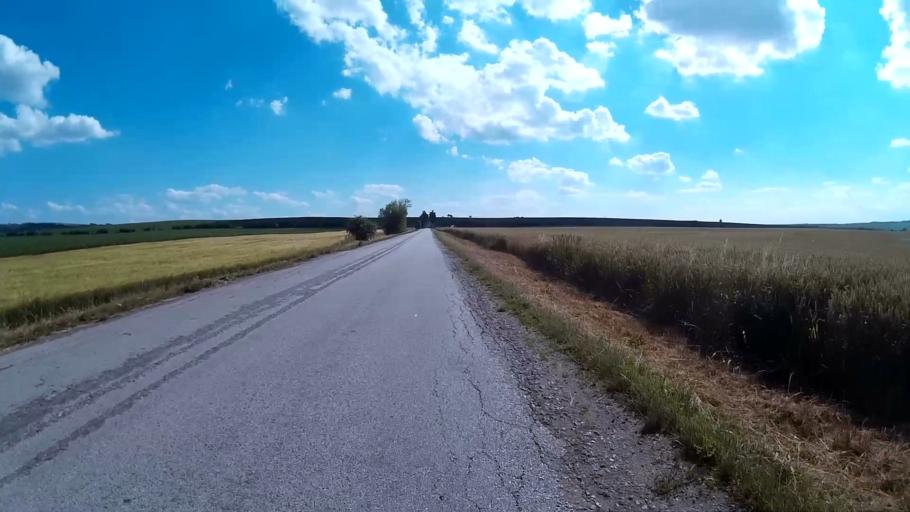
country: CZ
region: South Moravian
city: Krepice
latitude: 49.0261
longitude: 16.7135
